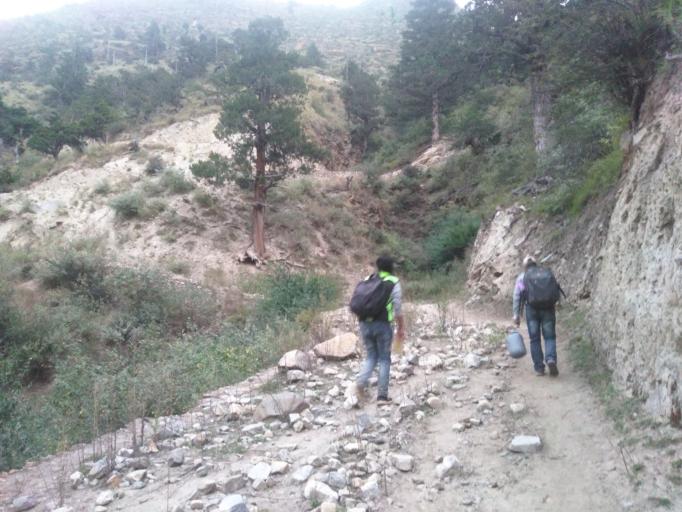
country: NP
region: Western Region
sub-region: Dhawalagiri Zone
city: Jomsom
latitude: 28.8840
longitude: 83.0259
